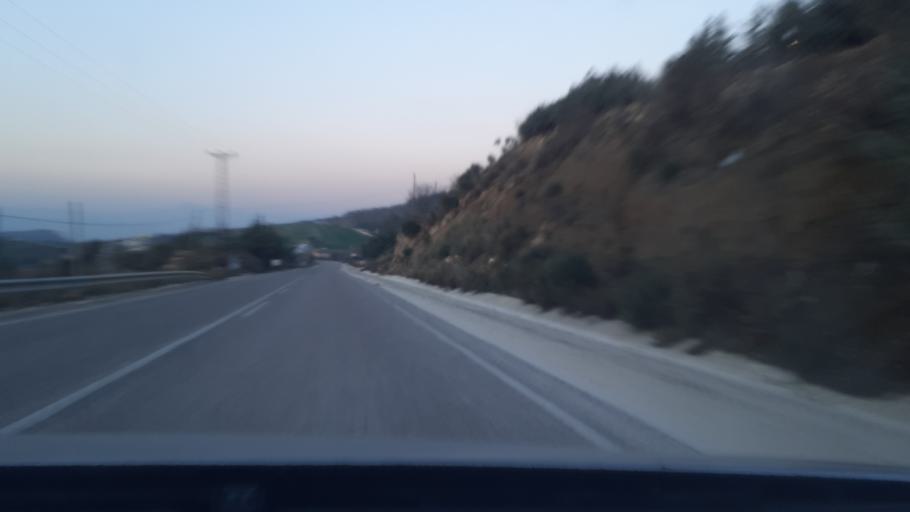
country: TR
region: Hatay
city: Dursunlu
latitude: 36.1758
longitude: 36.1879
